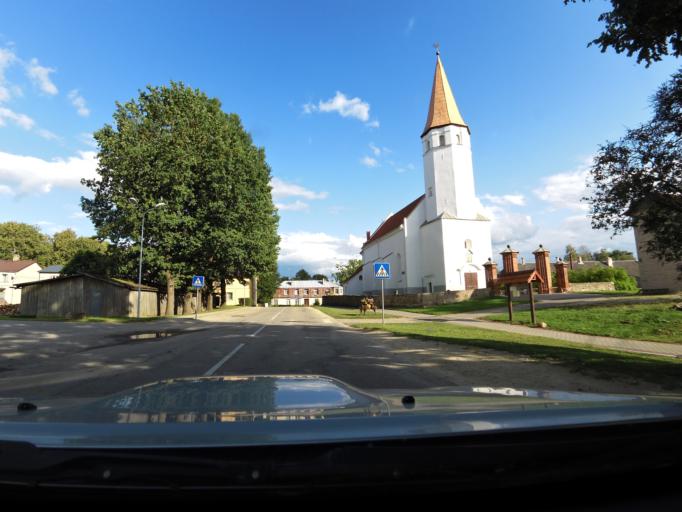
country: LV
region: Nereta
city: Nereta
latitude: 56.2052
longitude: 25.3067
